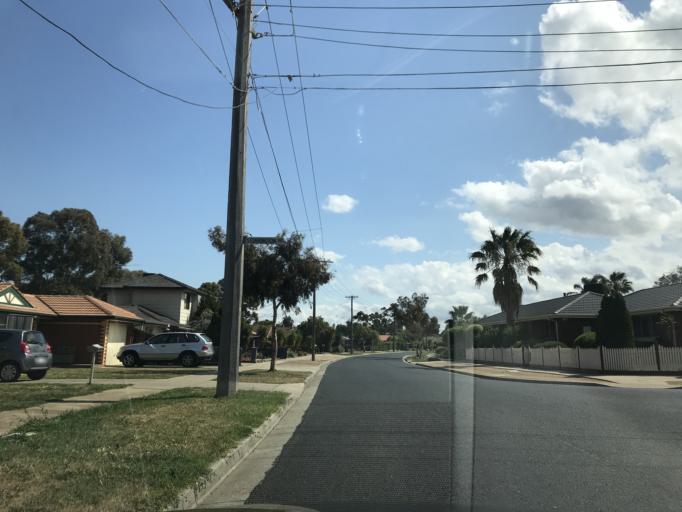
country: AU
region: Victoria
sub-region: Wyndham
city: Hoppers Crossing
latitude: -37.8687
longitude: 144.7068
